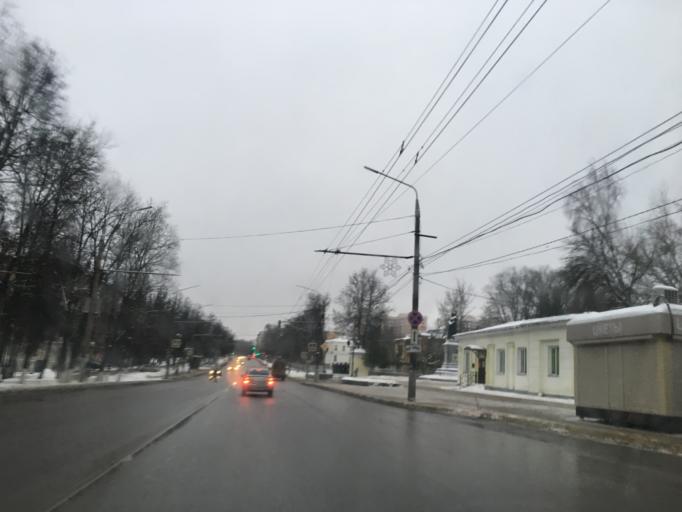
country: RU
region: Tula
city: Tula
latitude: 54.1844
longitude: 37.5962
